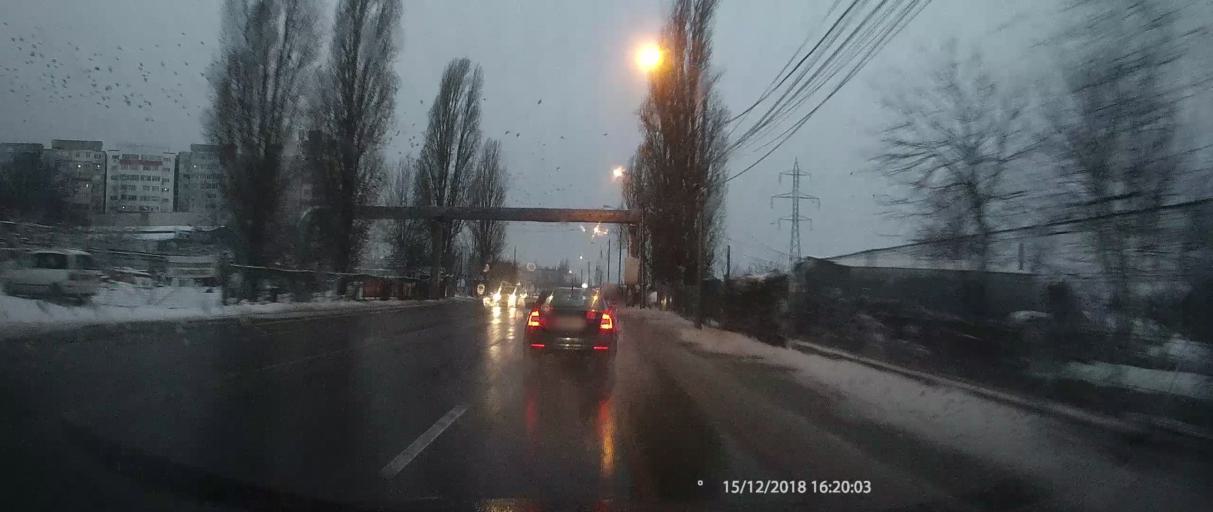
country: RO
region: Galati
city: Galati
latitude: 45.4155
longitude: 28.0049
